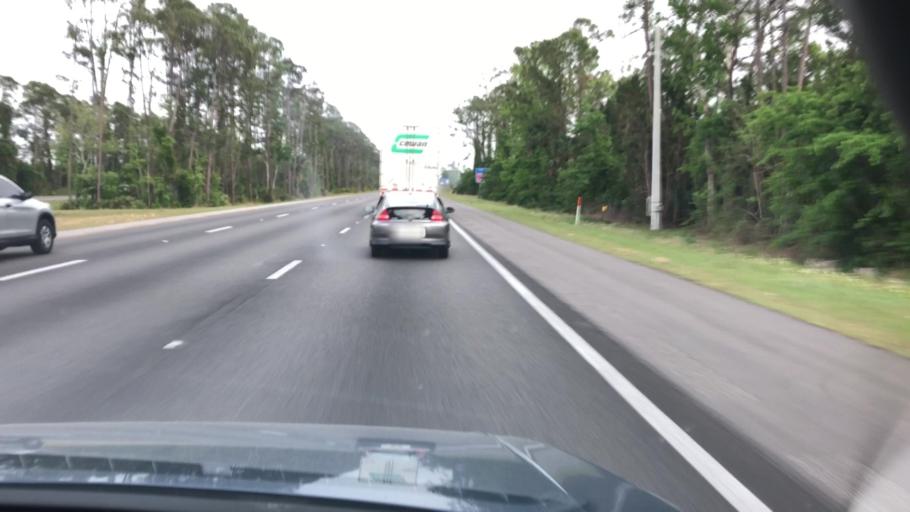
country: US
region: Florida
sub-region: Volusia County
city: Port Orange
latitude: 29.1177
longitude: -81.0407
